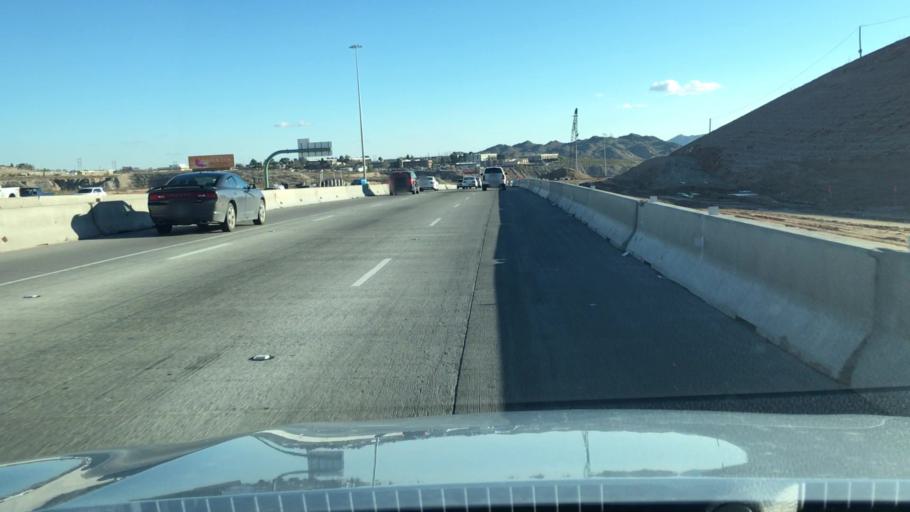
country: US
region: Texas
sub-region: El Paso County
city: El Paso
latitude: 31.8050
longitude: -106.5221
